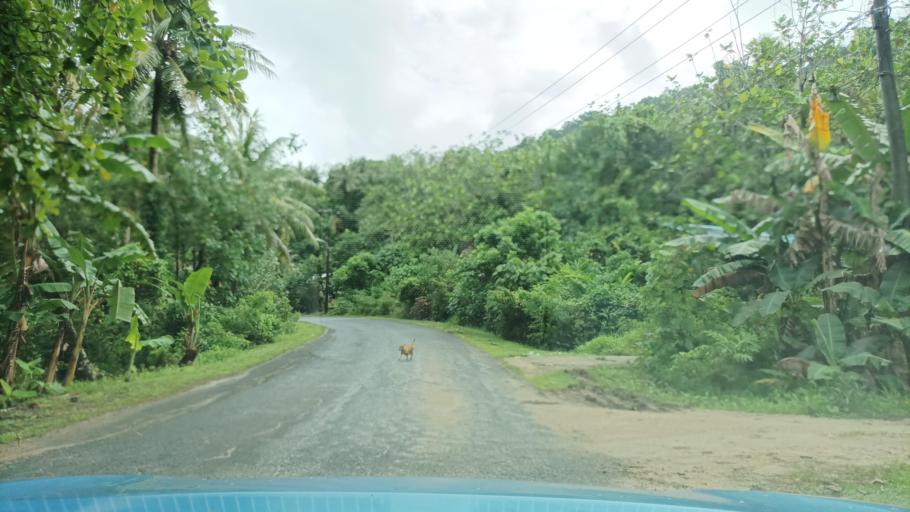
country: FM
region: Pohnpei
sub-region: Kolonia Municipality
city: Kolonia
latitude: 6.9606
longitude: 158.2491
